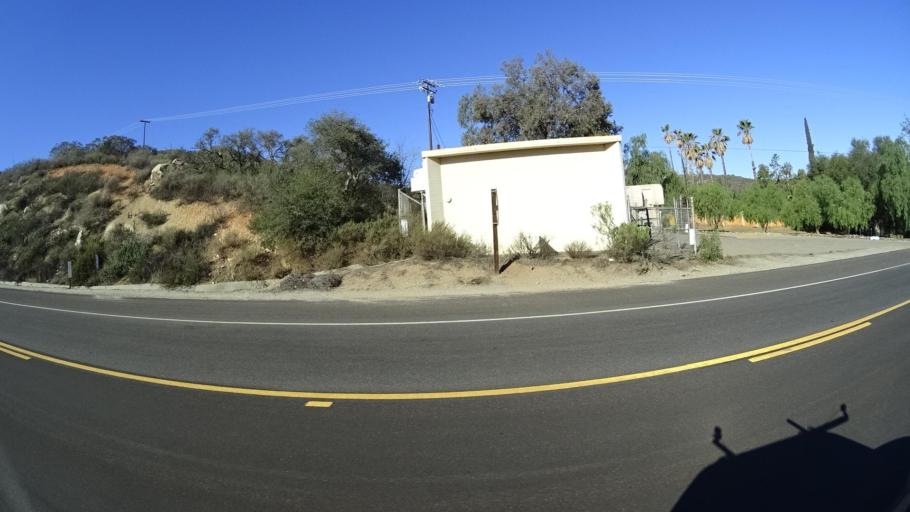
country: MX
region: Baja California
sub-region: Tijuana
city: Villa del Campo
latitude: 32.6276
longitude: -116.7649
